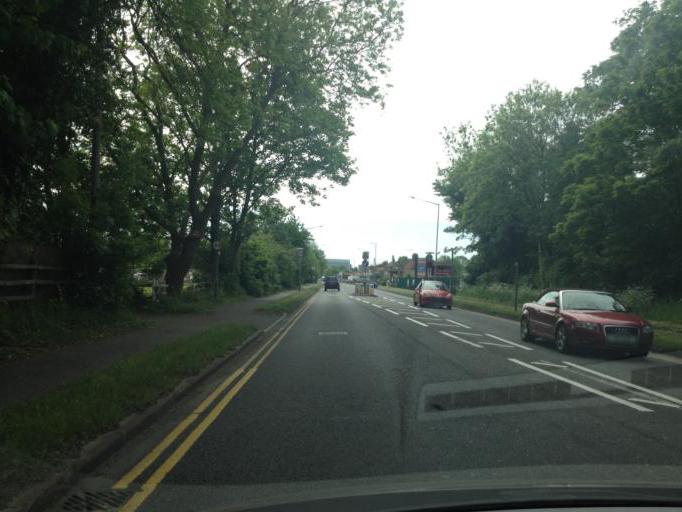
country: GB
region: England
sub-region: Greater London
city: Uxbridge
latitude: 51.5570
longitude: -0.4915
